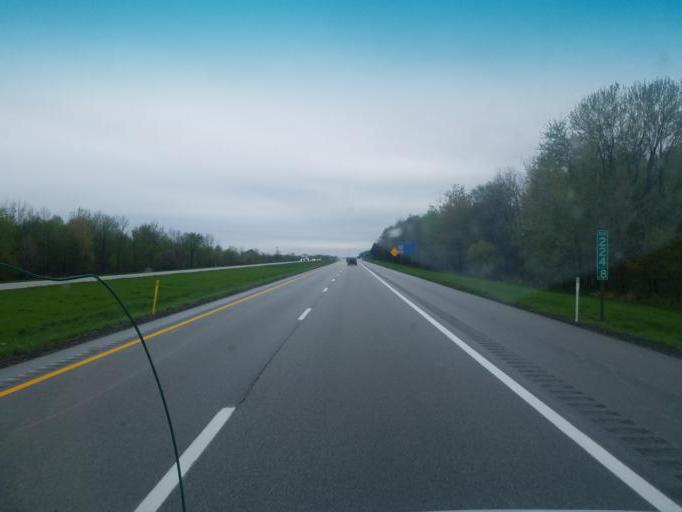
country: US
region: Ohio
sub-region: Ashtabula County
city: Ashtabula
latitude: 41.8015
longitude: -80.8305
